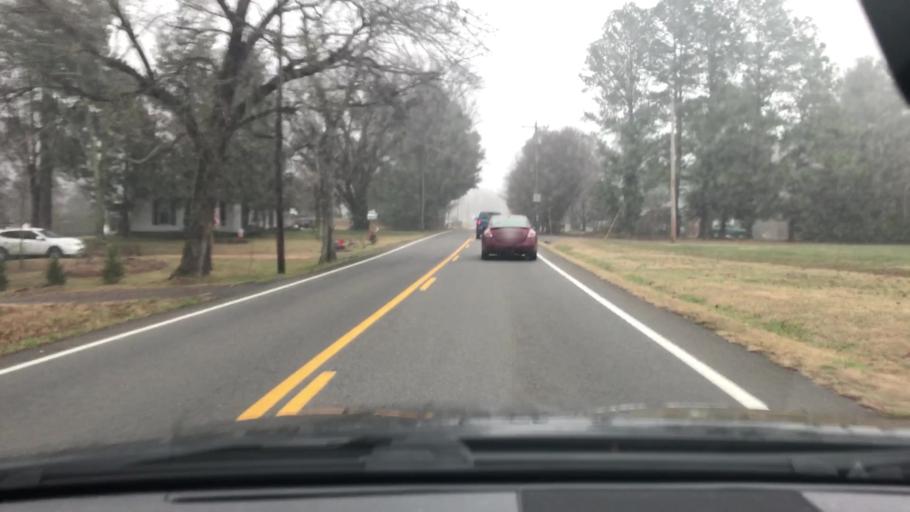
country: US
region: Tennessee
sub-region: Cheatham County
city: Ashland City
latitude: 36.2853
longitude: -87.1731
